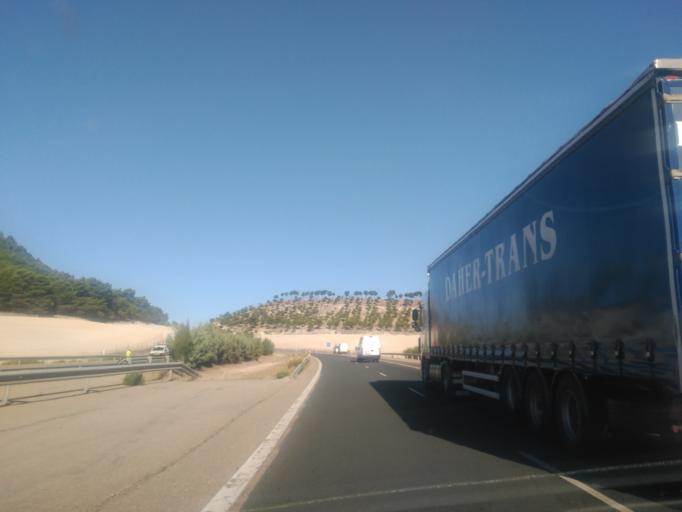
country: ES
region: Castille and Leon
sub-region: Provincia de Valladolid
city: Cisterniga
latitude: 41.6053
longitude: -4.6640
